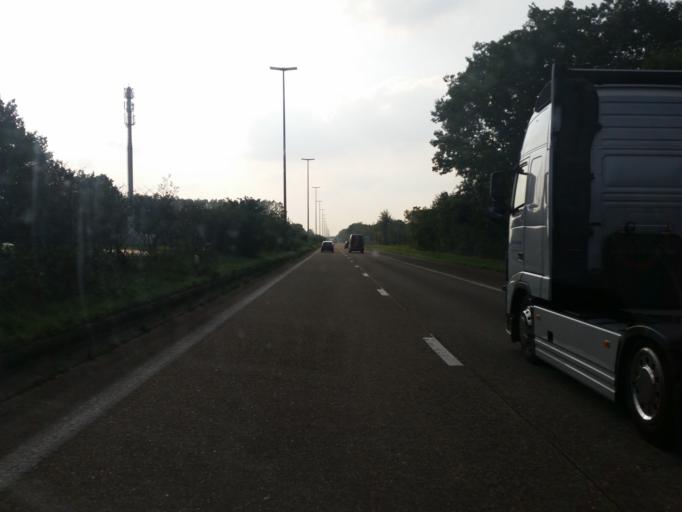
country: BE
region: Flanders
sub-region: Provincie Antwerpen
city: Turnhout
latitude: 51.2982
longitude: 4.9509
